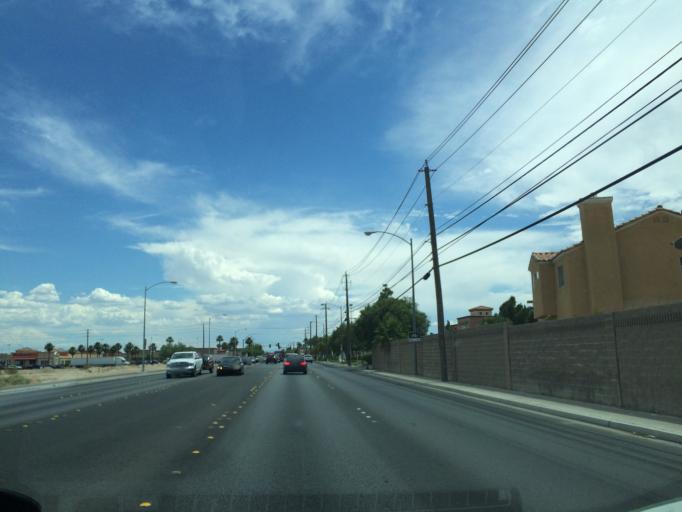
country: US
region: Nevada
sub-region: Clark County
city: North Las Vegas
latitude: 36.2418
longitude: -115.1711
